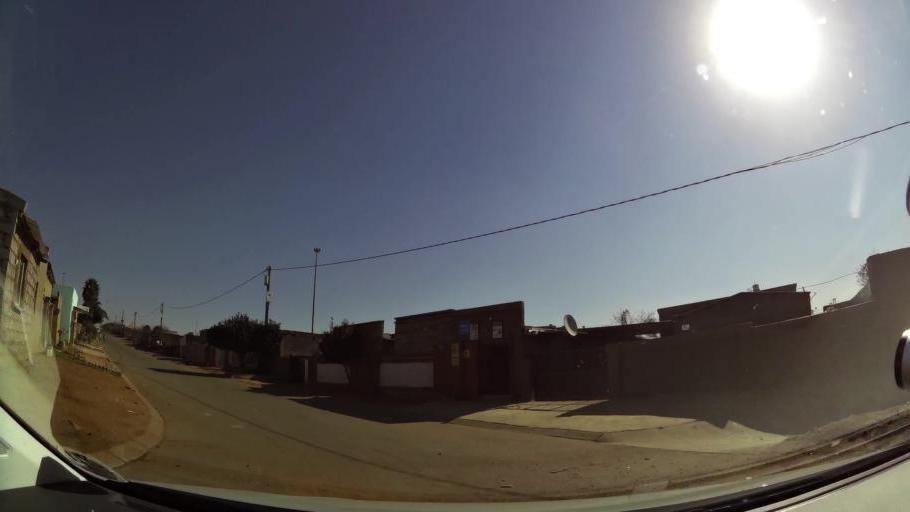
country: ZA
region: Gauteng
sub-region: Ekurhuleni Metropolitan Municipality
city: Tembisa
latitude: -26.0216
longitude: 28.2421
